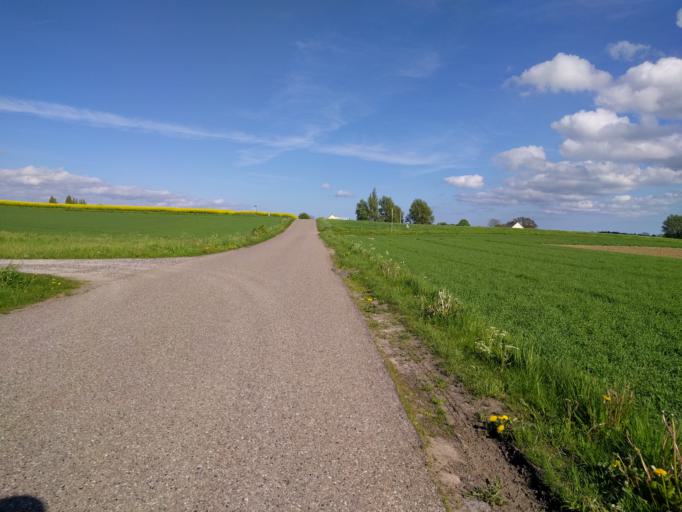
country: DK
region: Zealand
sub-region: Guldborgsund Kommune
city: Stubbekobing
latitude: 54.9261
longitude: 12.0259
